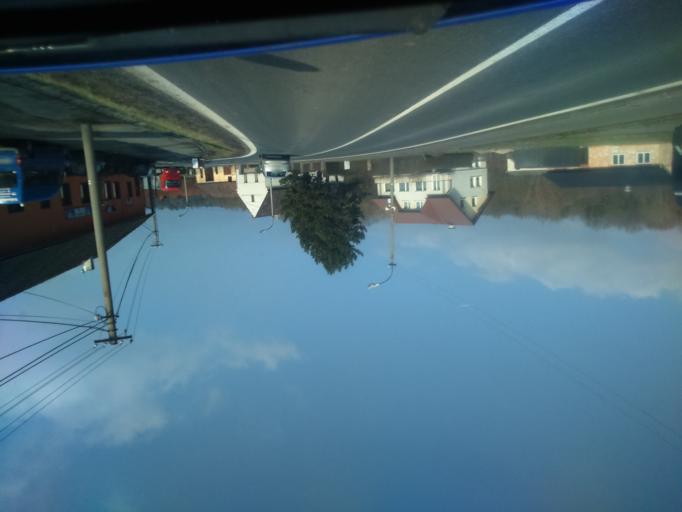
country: CZ
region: Plzensky
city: Horsovsky Tyn
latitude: 49.5390
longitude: 12.9815
